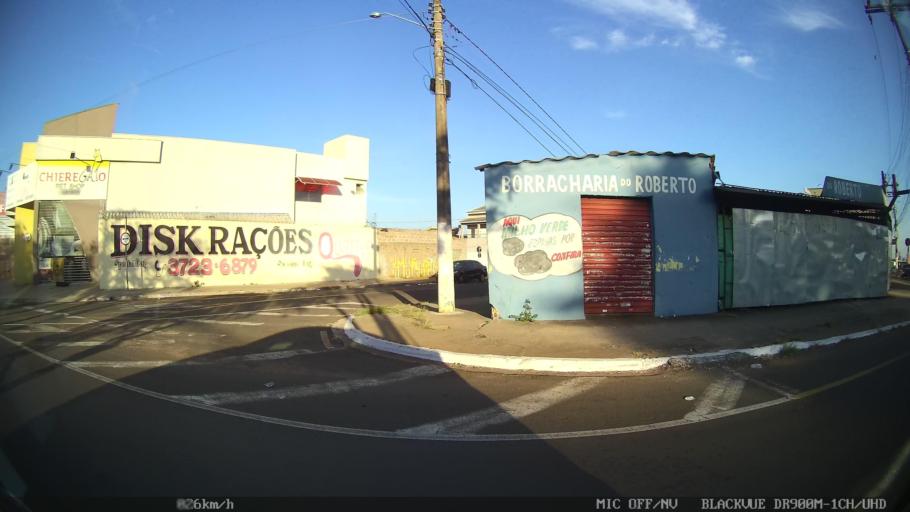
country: BR
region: Sao Paulo
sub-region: Franca
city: Franca
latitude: -20.5075
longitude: -47.3988
